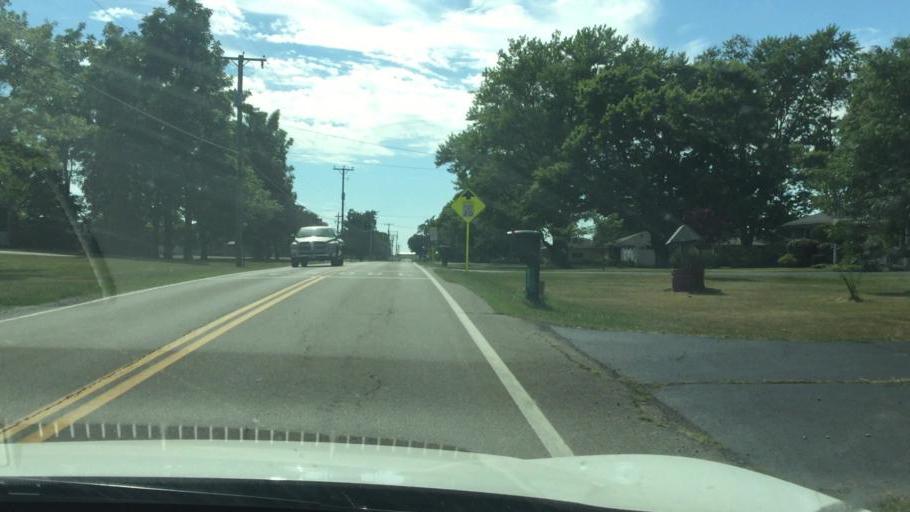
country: US
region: Ohio
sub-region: Clark County
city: Lisbon
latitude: 39.9419
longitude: -83.6774
